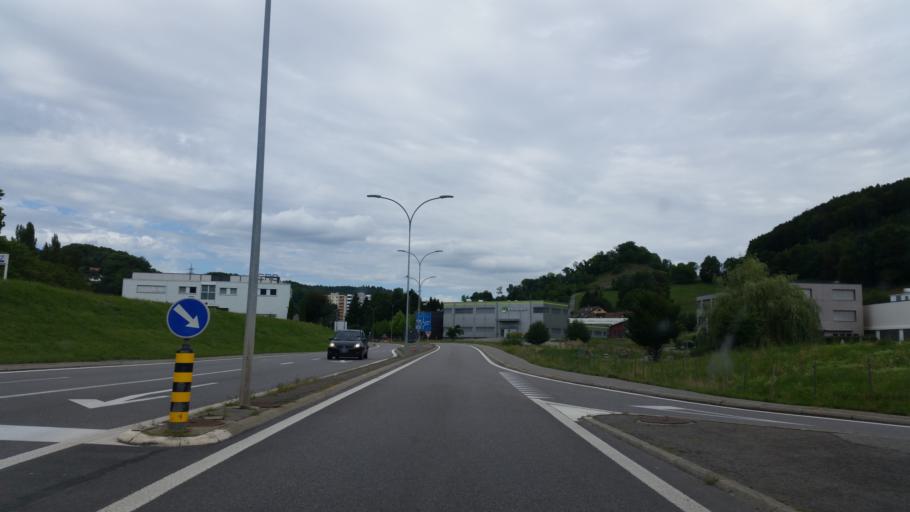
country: CH
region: Vaud
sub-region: Lavaux-Oron District
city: Chexbres
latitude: 46.4883
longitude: 6.7704
